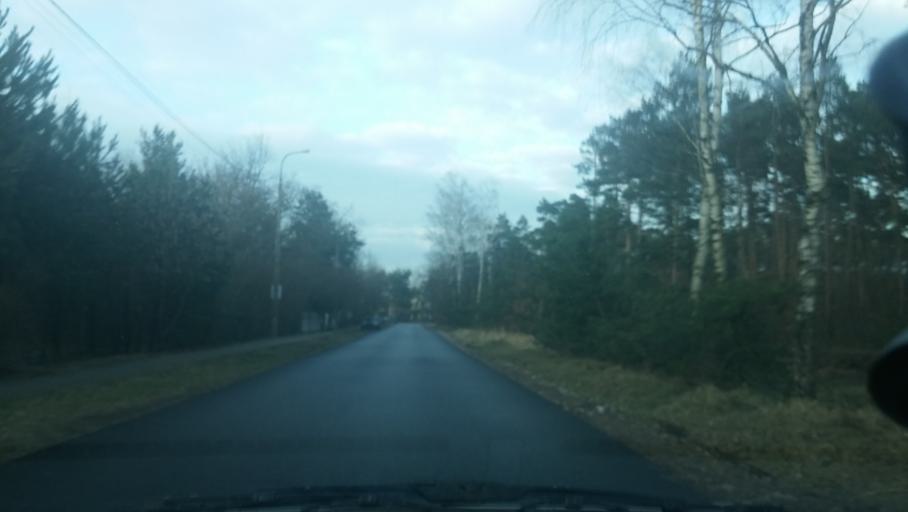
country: PL
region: Masovian Voivodeship
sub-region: Warszawa
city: Wawer
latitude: 52.1993
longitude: 21.1699
